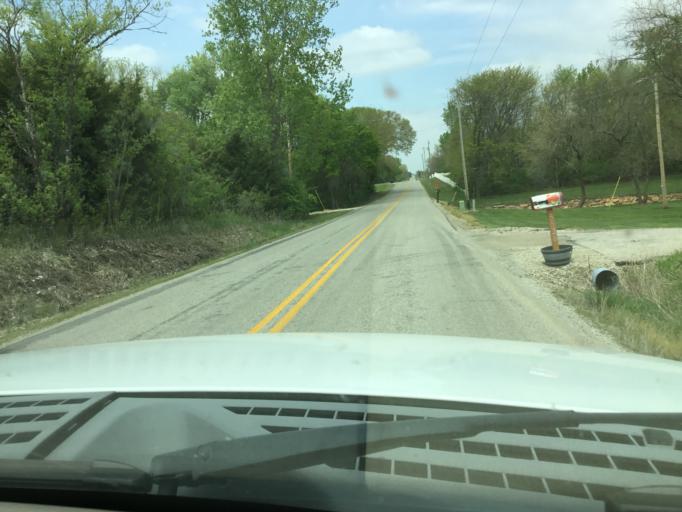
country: US
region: Kansas
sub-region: Shawnee County
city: Topeka
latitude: 38.9675
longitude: -95.6142
